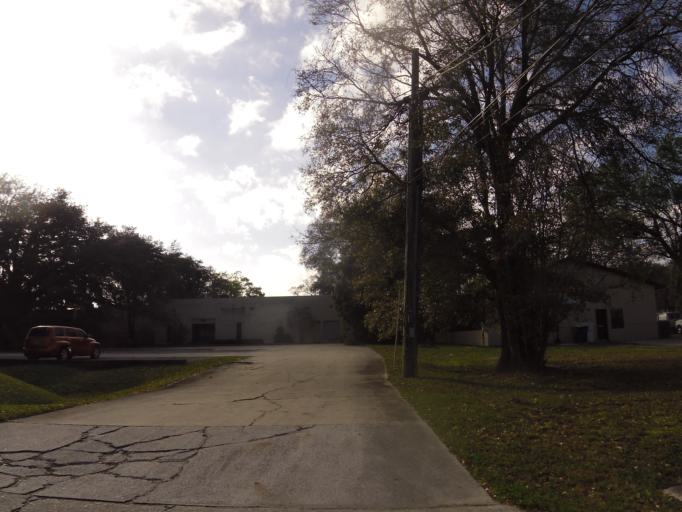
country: US
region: Florida
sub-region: Duval County
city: Jacksonville
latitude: 30.2916
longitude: -81.6226
